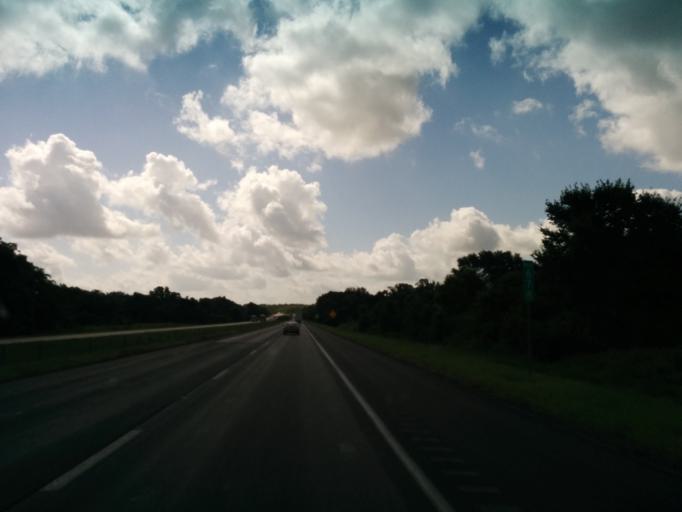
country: US
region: Texas
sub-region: Fayette County
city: Schulenburg
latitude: 29.6918
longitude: -96.8431
